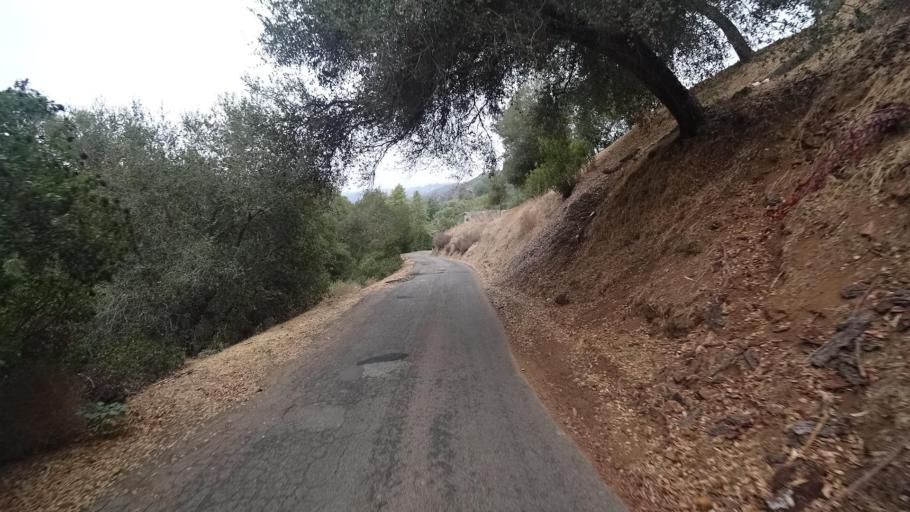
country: US
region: California
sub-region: San Diego County
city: Rainbow
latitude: 33.3776
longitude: -117.1588
